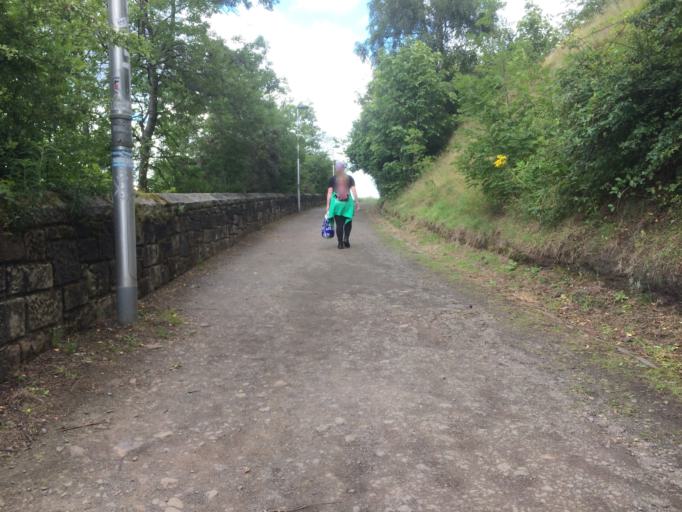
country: GB
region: Scotland
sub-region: Edinburgh
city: Edinburgh
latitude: 55.9552
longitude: -3.1847
